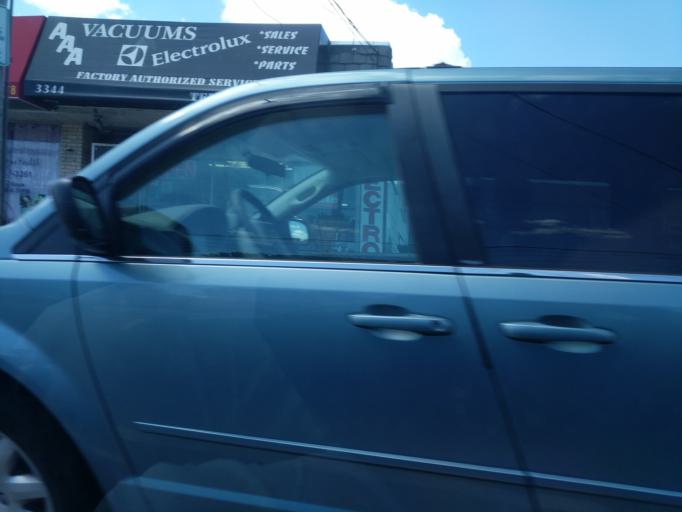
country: US
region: New York
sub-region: Nassau County
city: Oceanside
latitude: 40.6295
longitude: -73.6410
